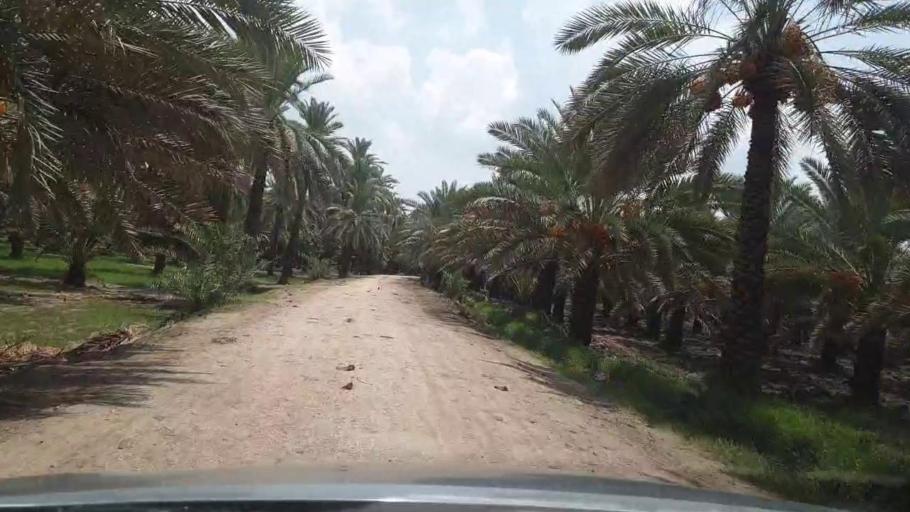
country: PK
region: Sindh
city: Khairpur
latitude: 27.6273
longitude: 68.7412
